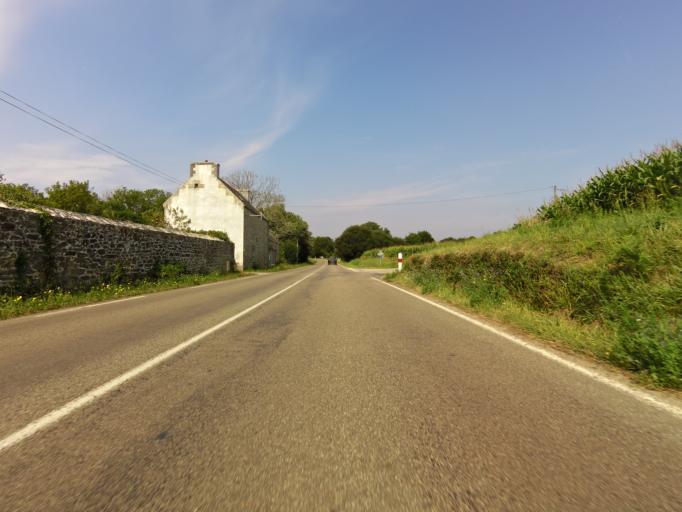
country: FR
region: Brittany
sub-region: Departement du Finistere
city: Esquibien
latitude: 48.0301
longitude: -4.5919
